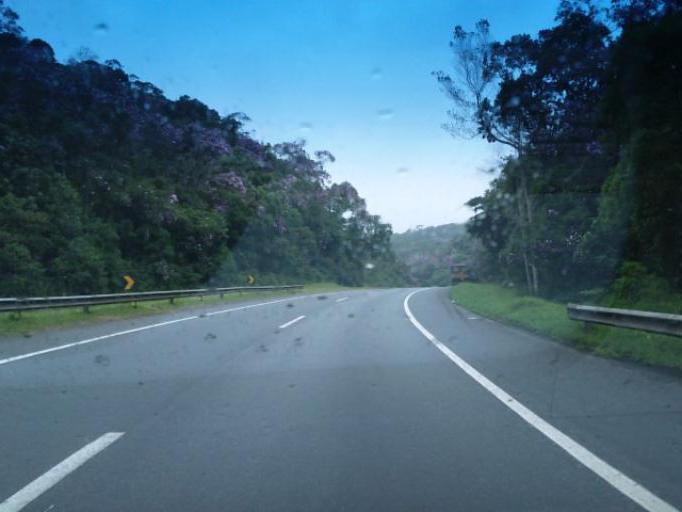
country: BR
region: Sao Paulo
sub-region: Cajati
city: Cajati
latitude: -24.9669
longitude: -48.4490
